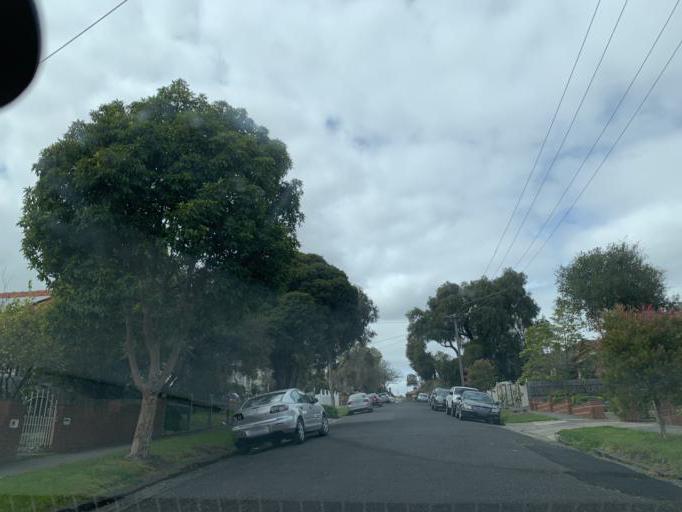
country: AU
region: Victoria
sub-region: Moreland
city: Coburg
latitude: -37.7535
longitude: 144.9550
